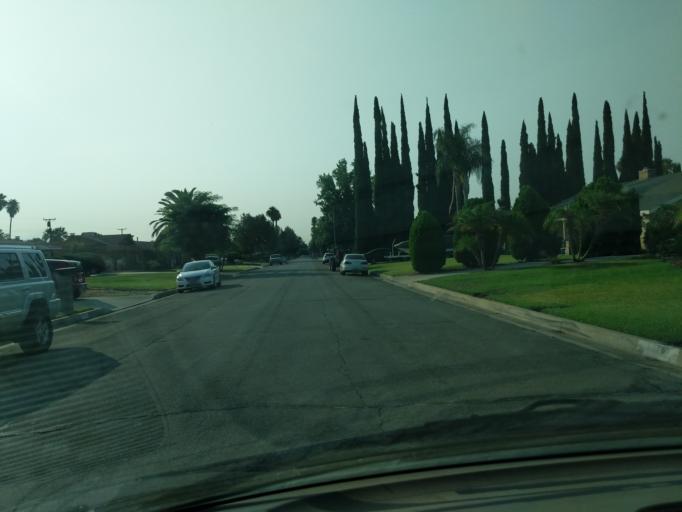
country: US
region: California
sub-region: San Bernardino County
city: Muscoy
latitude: 34.1485
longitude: -117.3848
